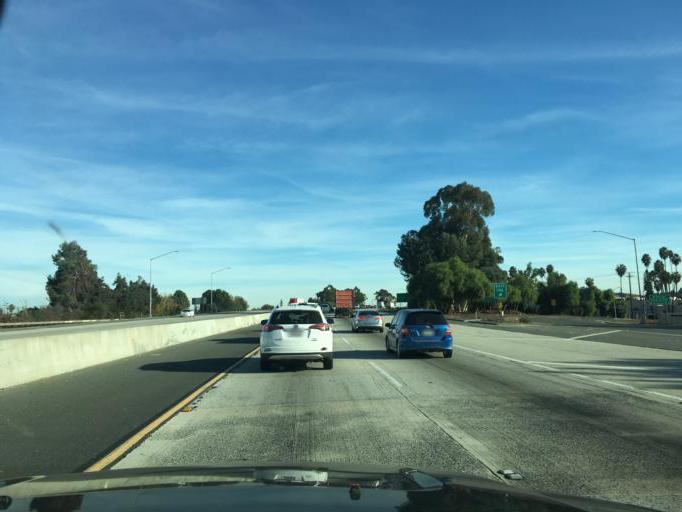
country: US
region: California
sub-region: Los Angeles County
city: Diamond Bar
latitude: 34.0631
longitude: -117.7926
